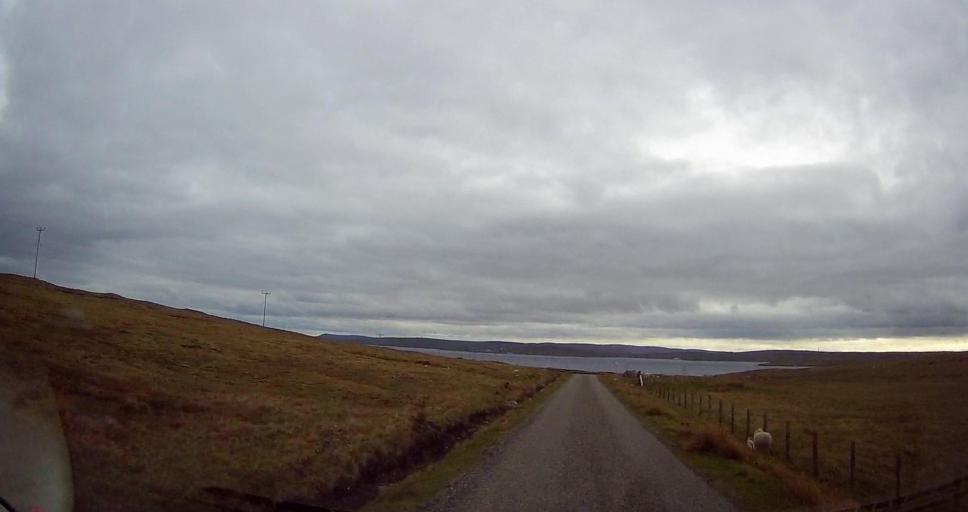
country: GB
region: Scotland
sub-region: Shetland Islands
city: Shetland
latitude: 60.5035
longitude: -1.1477
